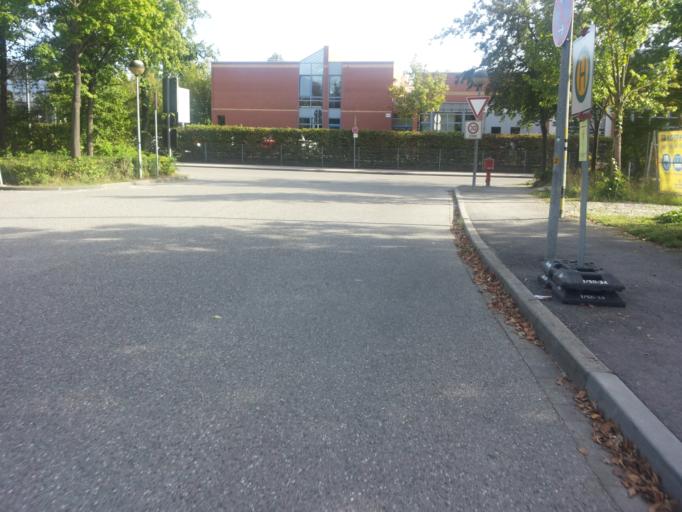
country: DE
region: Bavaria
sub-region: Upper Bavaria
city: Ingolstadt
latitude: 48.7804
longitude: 11.4190
